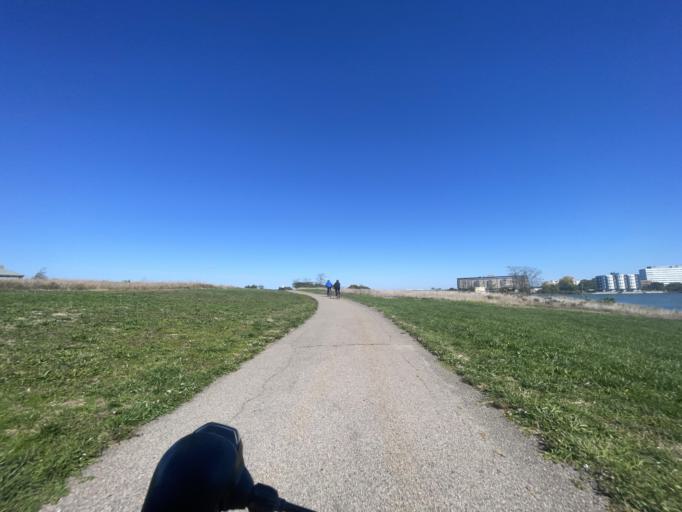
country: US
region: Massachusetts
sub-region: Norfolk County
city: Milton
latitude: 42.2782
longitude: -71.0434
